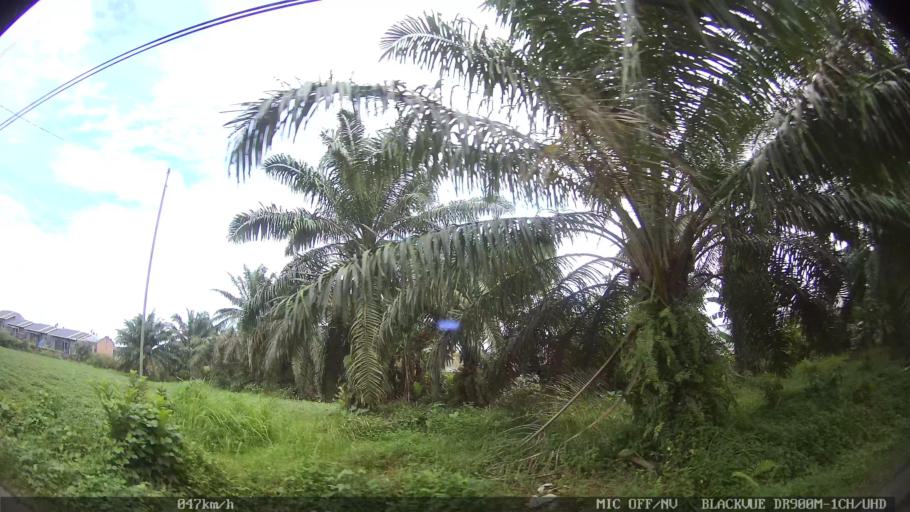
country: ID
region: North Sumatra
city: Sunggal
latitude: 3.5727
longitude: 98.5710
